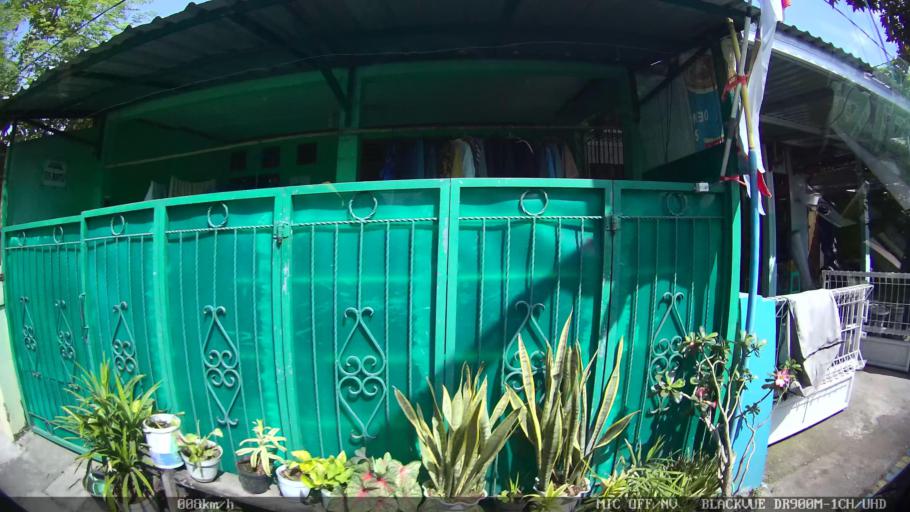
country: ID
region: Daerah Istimewa Yogyakarta
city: Kasihan
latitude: -7.8323
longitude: 110.3721
